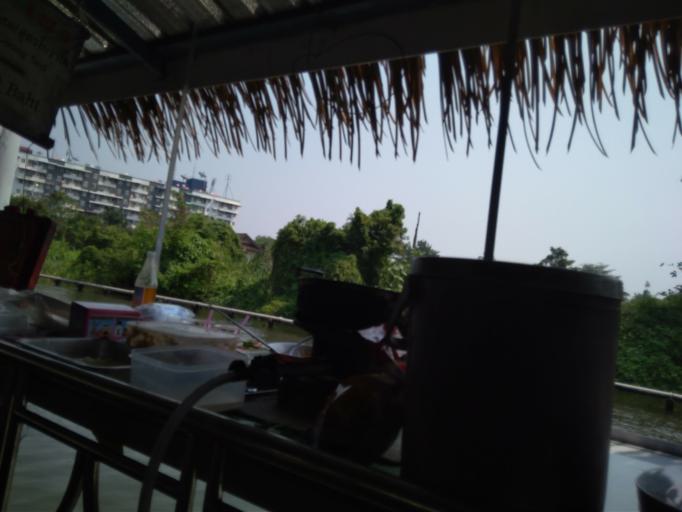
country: TH
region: Bangkok
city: Taling Chan
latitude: 13.7766
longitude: 100.4569
